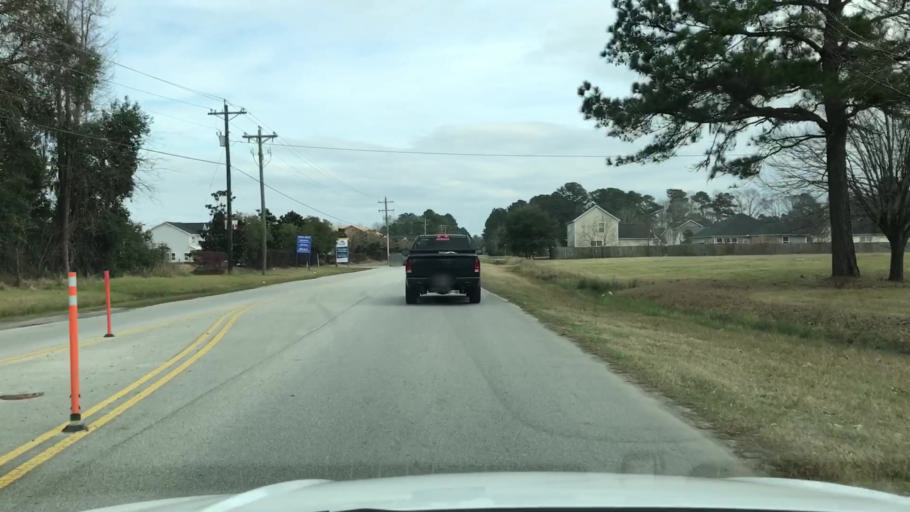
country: US
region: South Carolina
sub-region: Berkeley County
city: Goose Creek
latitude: 33.0329
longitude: -80.0316
